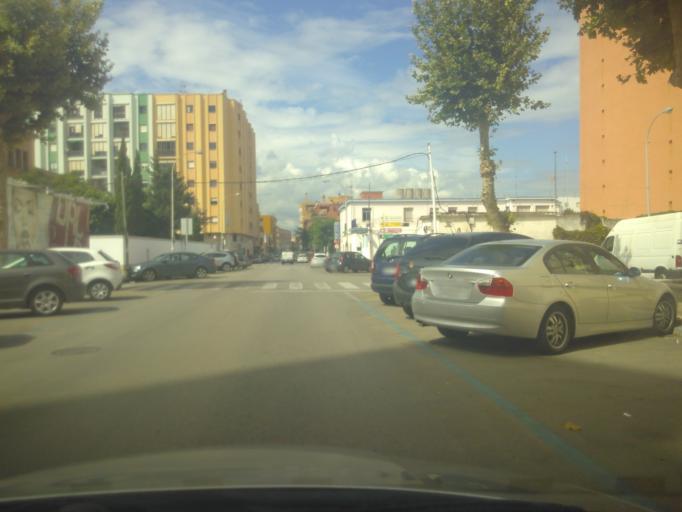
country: ES
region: Andalusia
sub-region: Provincia de Cadiz
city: La Linea de la Concepcion
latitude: 36.1606
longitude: -5.3473
